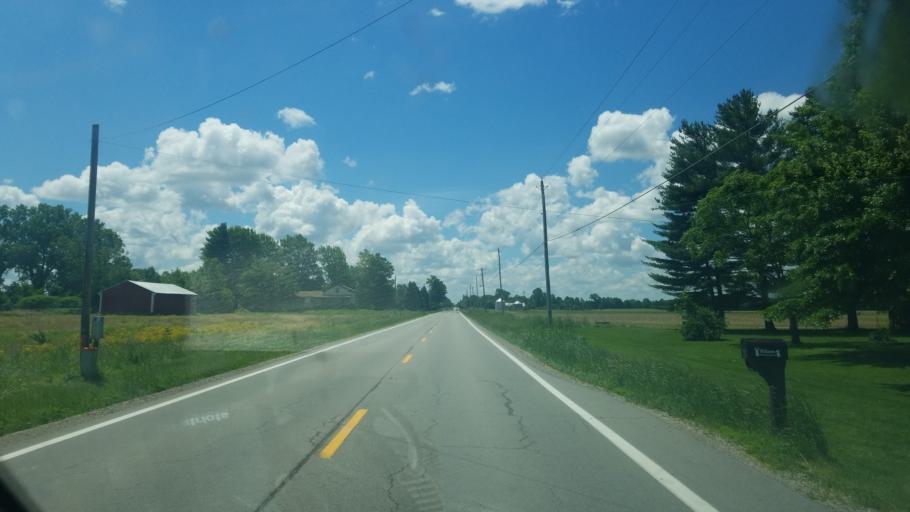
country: US
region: Ohio
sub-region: Huron County
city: Wakeman
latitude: 41.1774
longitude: -82.4106
